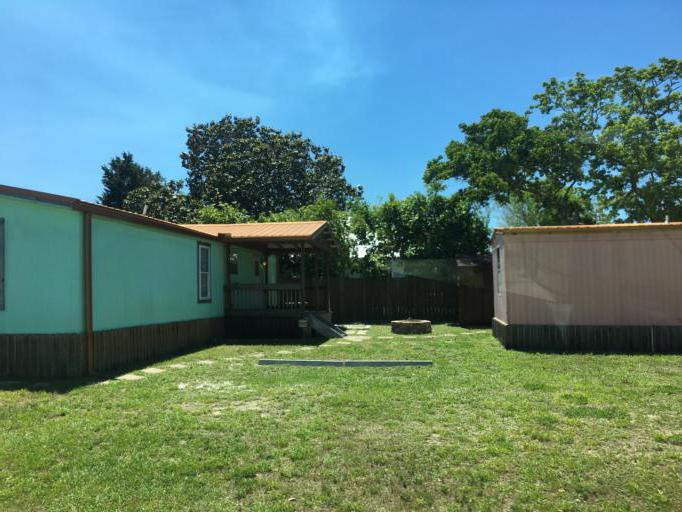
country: US
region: Florida
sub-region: Bay County
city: Laguna Beach
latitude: 30.2429
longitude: -85.9227
